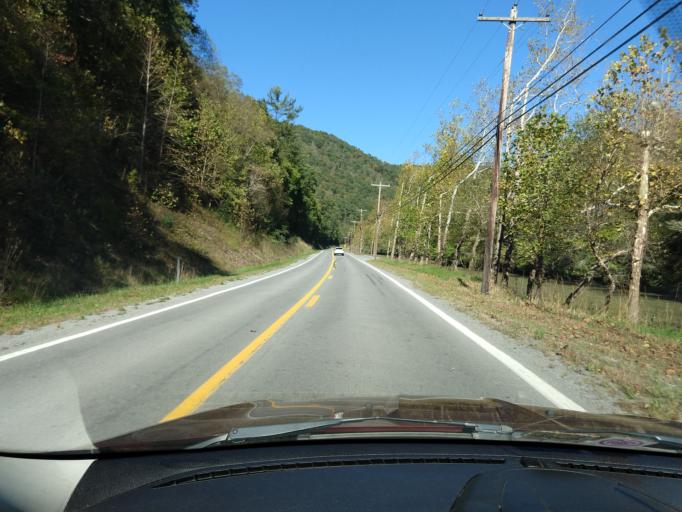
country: US
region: West Virginia
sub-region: Pocahontas County
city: Marlinton
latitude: 38.2104
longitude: -80.0493
